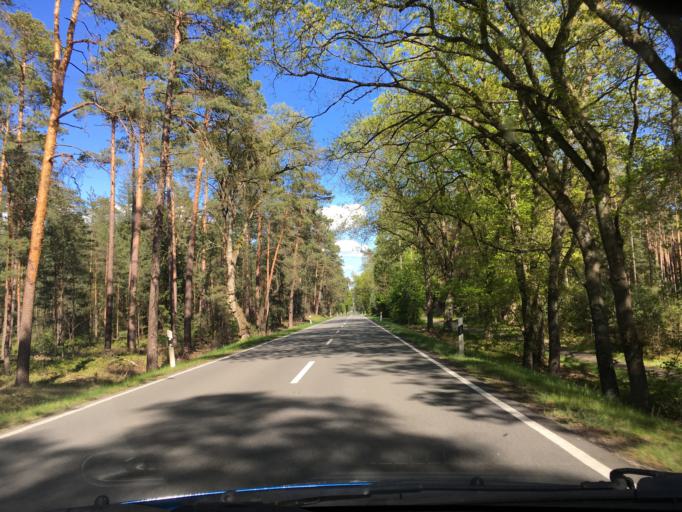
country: DE
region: Lower Saxony
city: Prezelle
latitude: 53.0143
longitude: 11.4075
